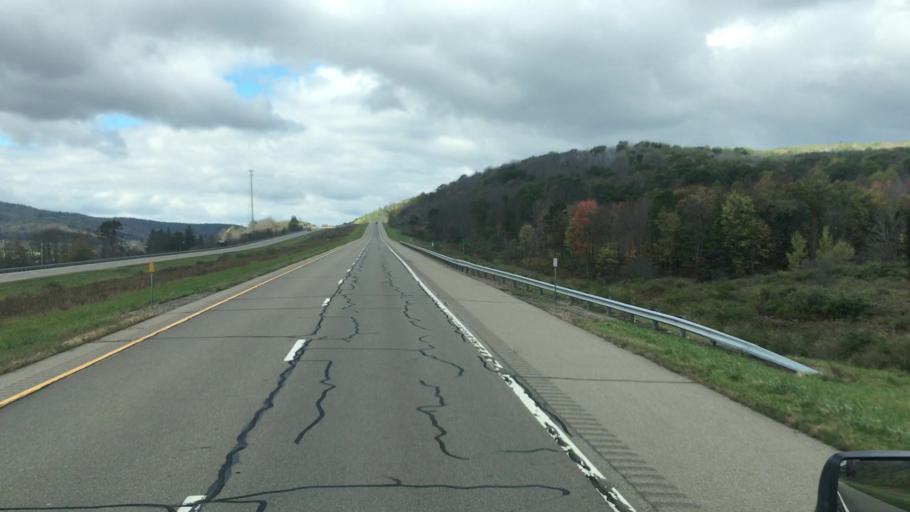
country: US
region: New York
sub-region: Allegany County
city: Friendship
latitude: 42.2073
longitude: -78.1873
